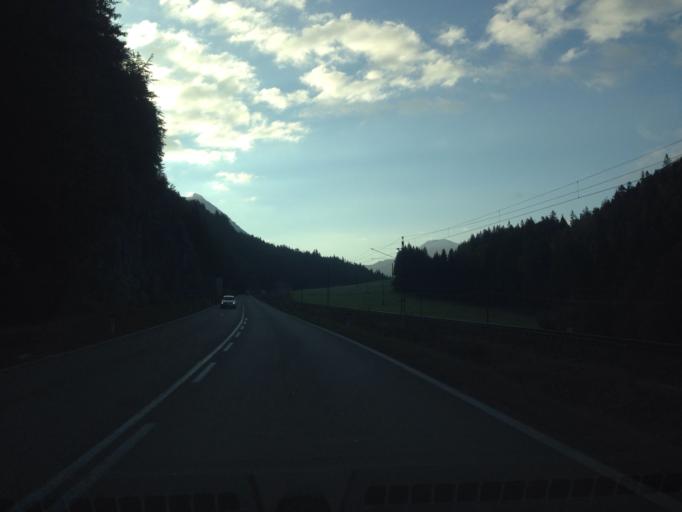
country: AT
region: Tyrol
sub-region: Politischer Bezirk Reutte
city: Heiterwang
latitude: 47.4561
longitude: 10.7247
